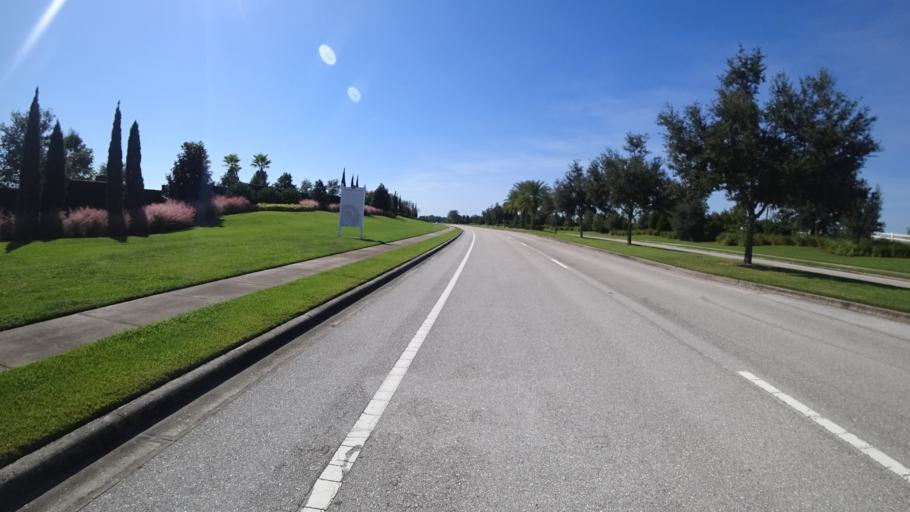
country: US
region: Florida
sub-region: Sarasota County
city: The Meadows
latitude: 27.4024
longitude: -82.3763
